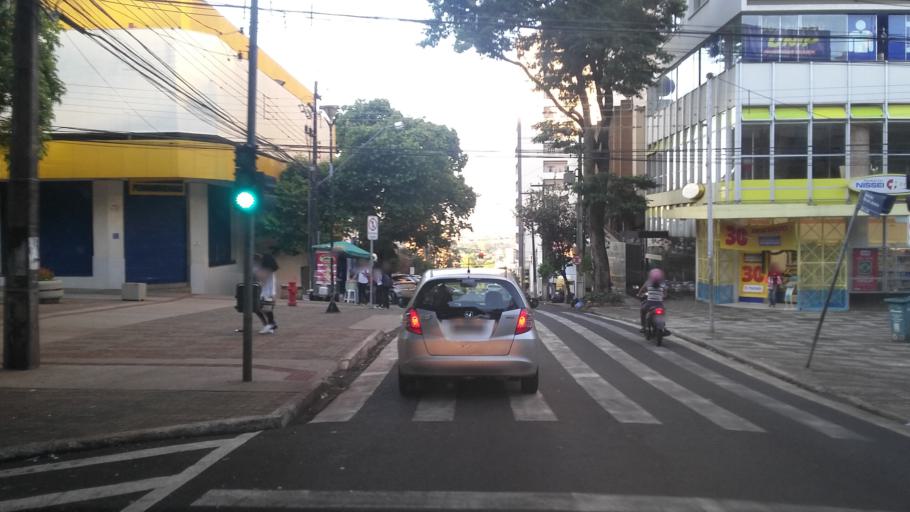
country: BR
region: Parana
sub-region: Londrina
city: Londrina
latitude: -23.3111
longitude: -51.1590
